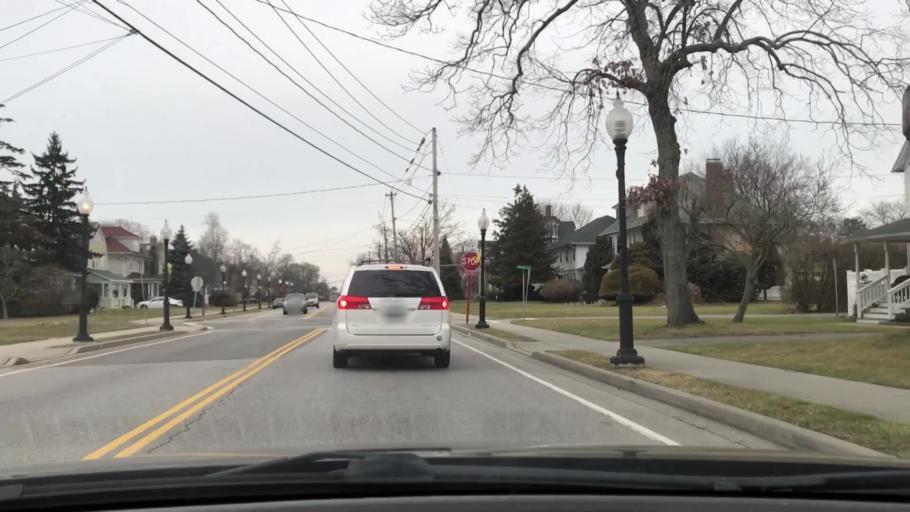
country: US
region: New York
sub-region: Suffolk County
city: Patchogue
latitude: 40.7710
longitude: -73.0150
